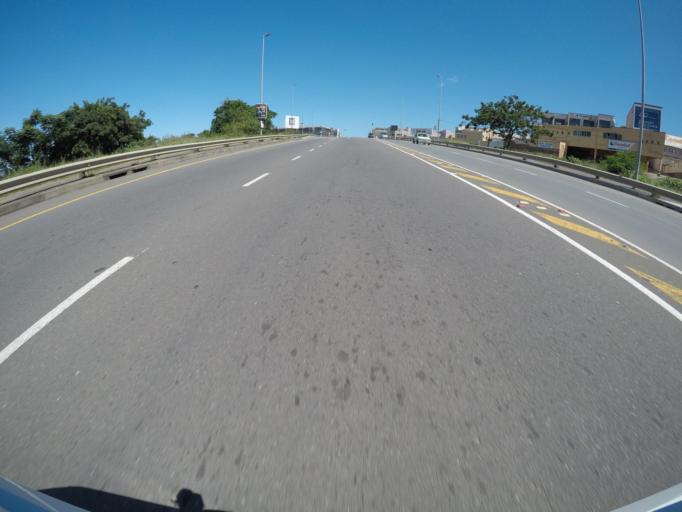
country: ZA
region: Eastern Cape
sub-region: Buffalo City Metropolitan Municipality
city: East London
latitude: -33.0059
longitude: 27.9132
